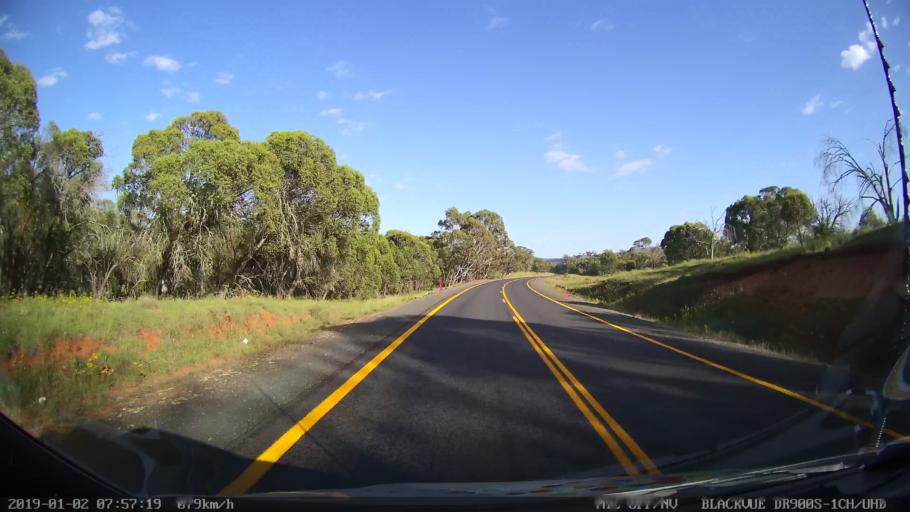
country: AU
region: New South Wales
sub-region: Tumut Shire
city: Tumut
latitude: -35.6650
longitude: 148.4747
